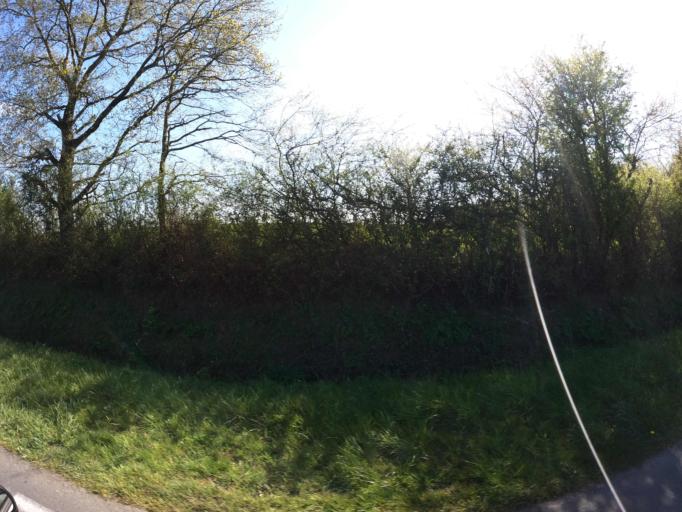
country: FR
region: Pays de la Loire
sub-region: Departement de Maine-et-Loire
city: La Seguiniere
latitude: 47.0733
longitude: -0.9257
